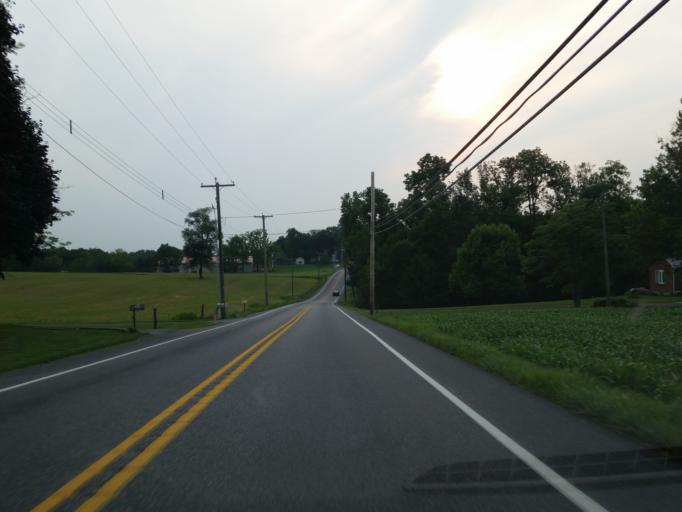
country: US
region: Pennsylvania
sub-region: Lebanon County
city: Annville
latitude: 40.3505
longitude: -76.5332
